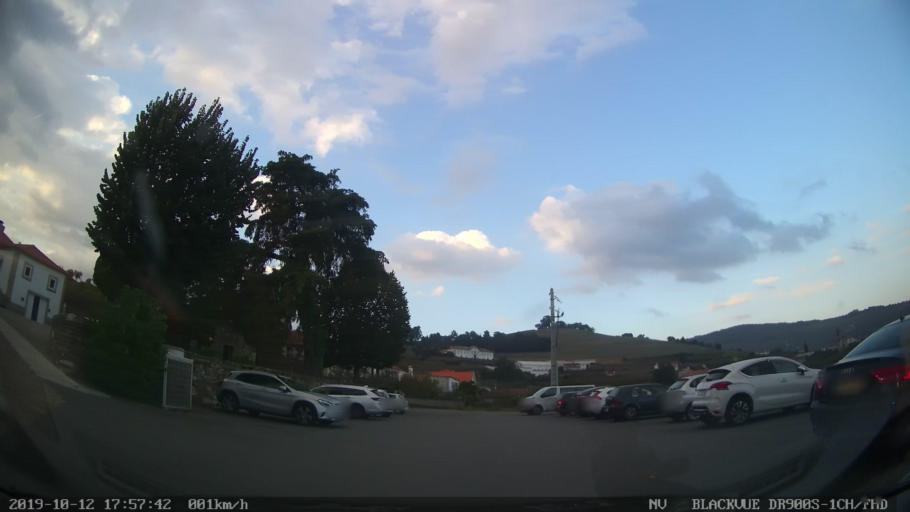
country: PT
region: Vila Real
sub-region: Mesao Frio
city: Mesao Frio
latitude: 41.1645
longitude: -7.8468
